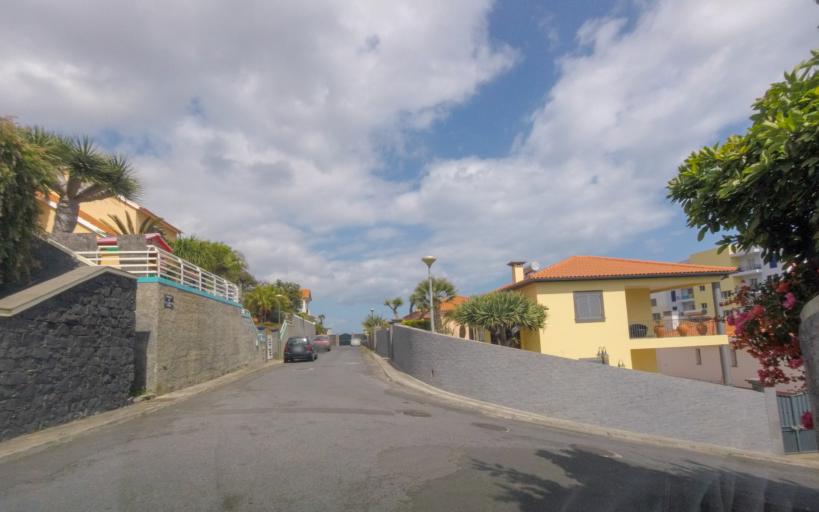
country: PT
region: Madeira
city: Camara de Lobos
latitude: 32.6503
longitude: -16.9395
